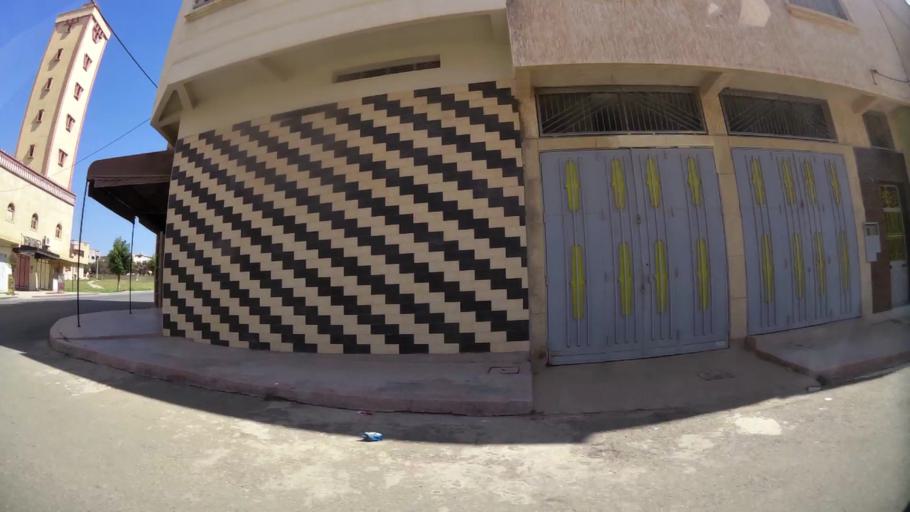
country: MA
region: Oriental
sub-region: Oujda-Angad
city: Oujda
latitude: 34.6740
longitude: -1.9411
